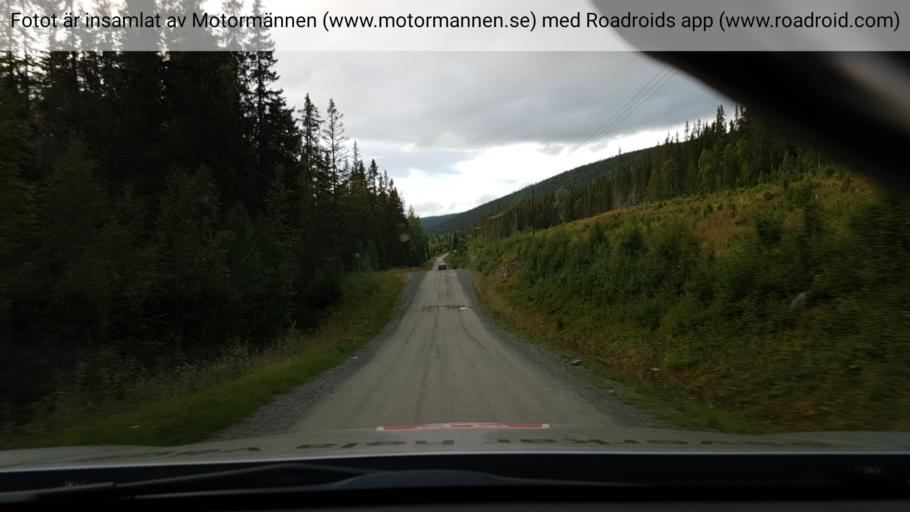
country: SE
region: Vaesterbotten
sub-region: Vilhelmina Kommun
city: Sjoberg
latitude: 65.5975
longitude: 15.2821
